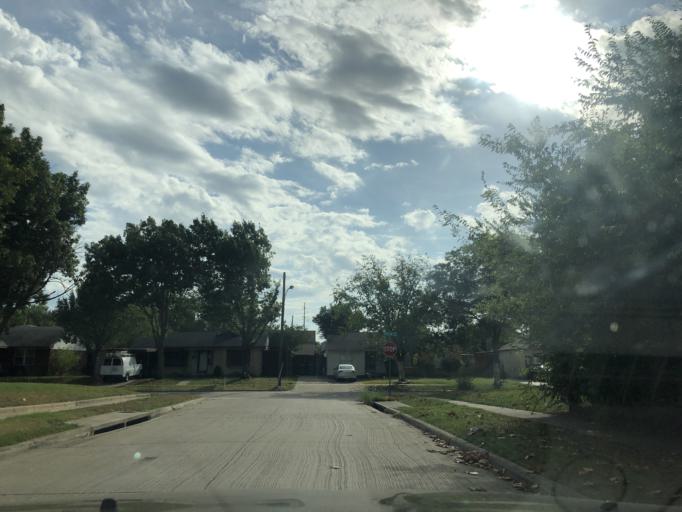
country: US
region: Texas
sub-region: Dallas County
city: Garland
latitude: 32.8816
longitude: -96.6621
